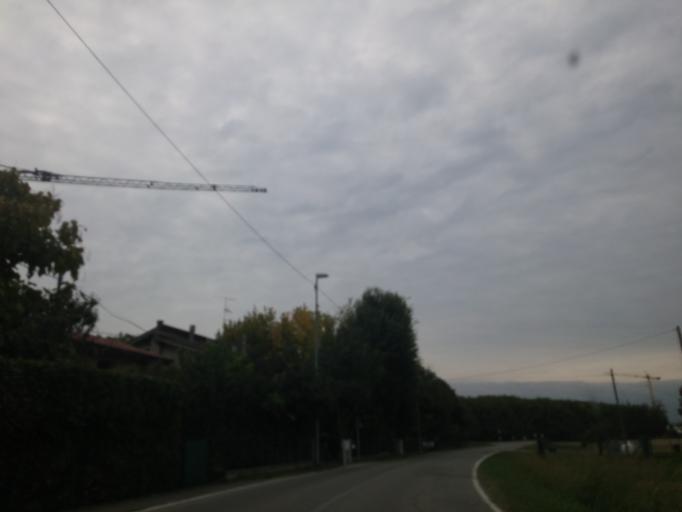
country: IT
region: Emilia-Romagna
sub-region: Provincia di Bologna
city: Longara
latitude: 44.5801
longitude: 11.3244
